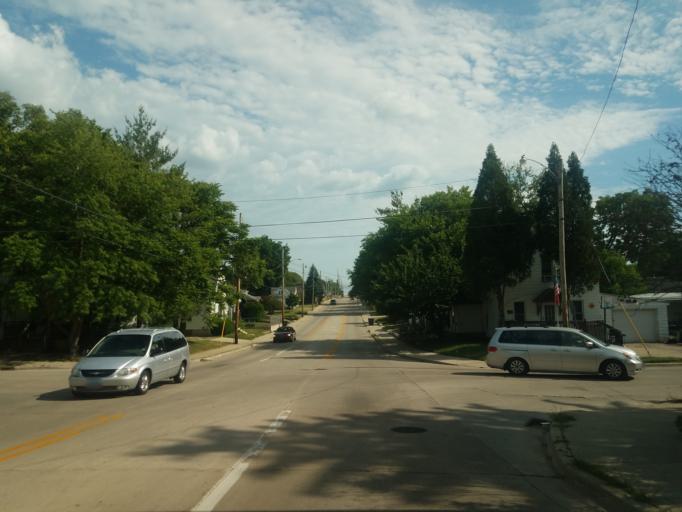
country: US
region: Illinois
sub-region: McLean County
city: Bloomington
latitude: 40.4770
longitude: -89.0066
